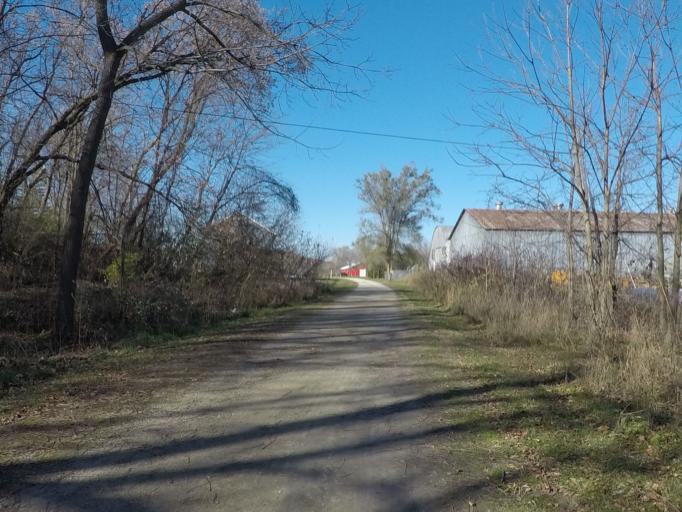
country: US
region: Wisconsin
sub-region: Dane County
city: Deerfield
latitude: 43.0548
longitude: -89.0718
